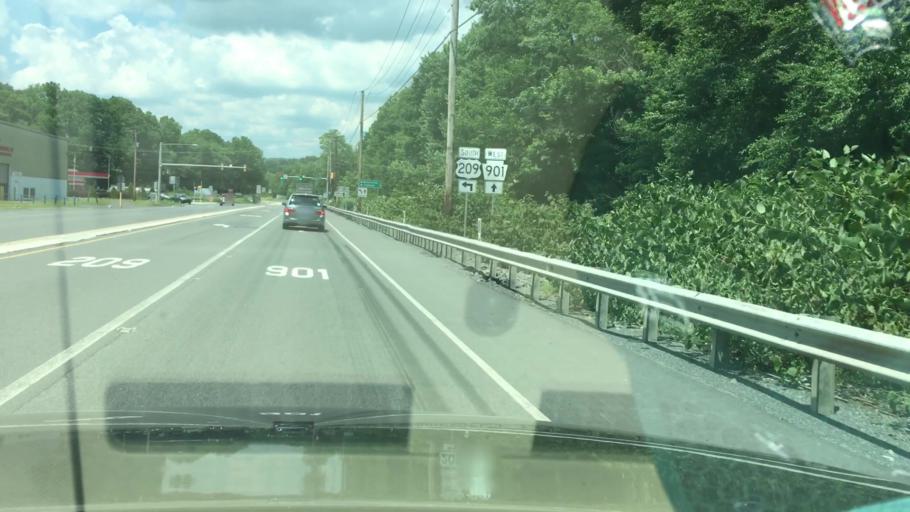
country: US
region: Pennsylvania
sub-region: Schuylkill County
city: Minersville
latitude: 40.6774
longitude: -76.2470
